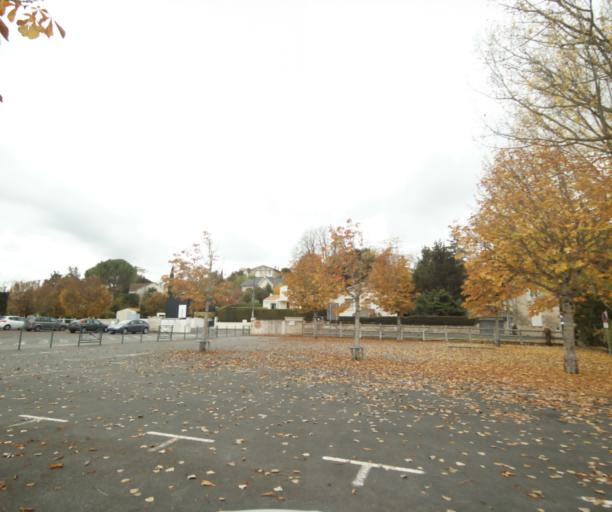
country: FR
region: Poitou-Charentes
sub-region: Departement de la Charente-Maritime
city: Saintes
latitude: 45.7552
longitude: -0.6282
